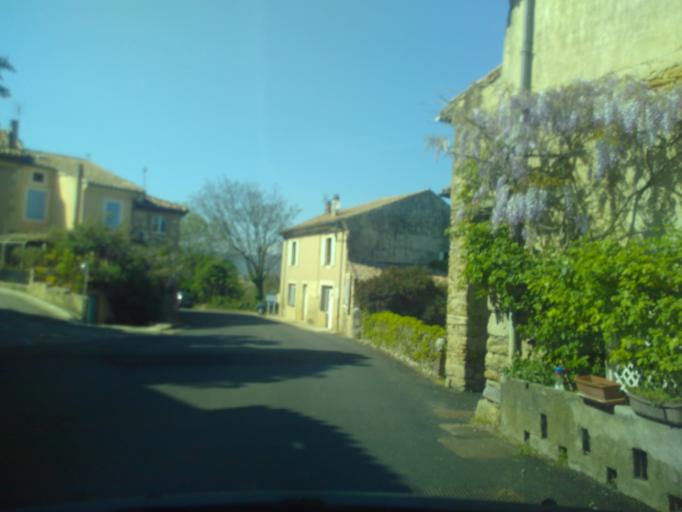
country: FR
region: Rhone-Alpes
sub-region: Departement de la Drome
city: La Begude-de-Mazenc
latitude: 44.5930
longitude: 4.9520
